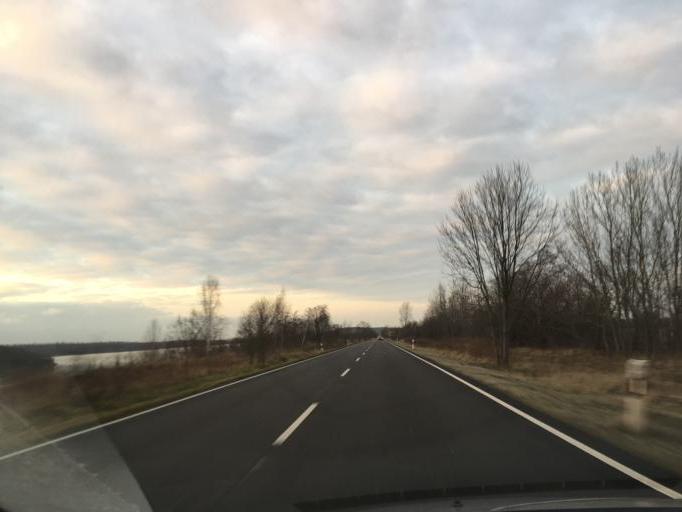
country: DE
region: Saxony
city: Espenhain
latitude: 51.2086
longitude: 12.4518
